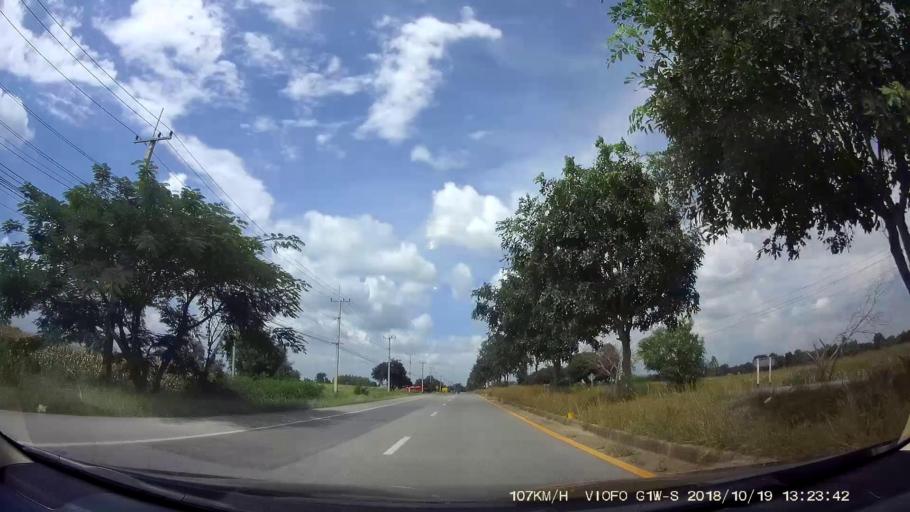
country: TH
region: Chaiyaphum
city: Chatturat
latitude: 15.4962
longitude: 101.8208
